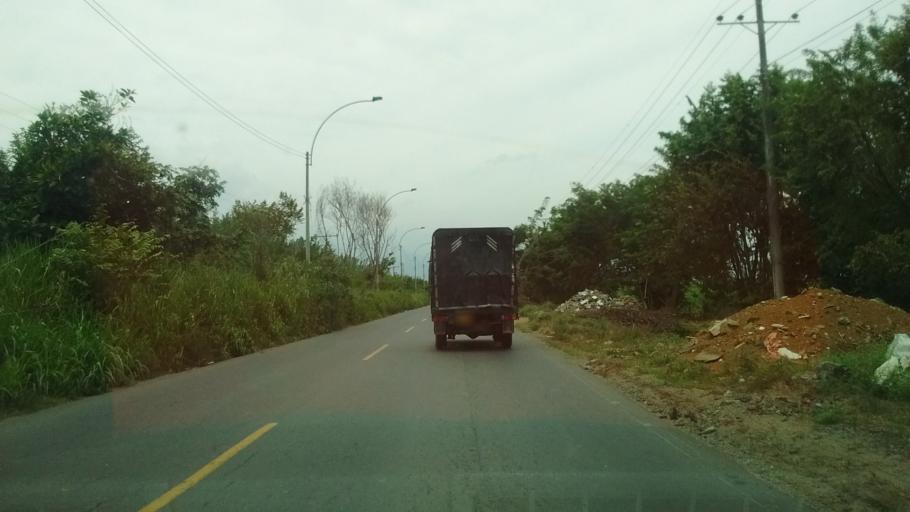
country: CO
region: Valle del Cauca
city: Jamundi
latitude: 3.3276
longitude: -76.5046
